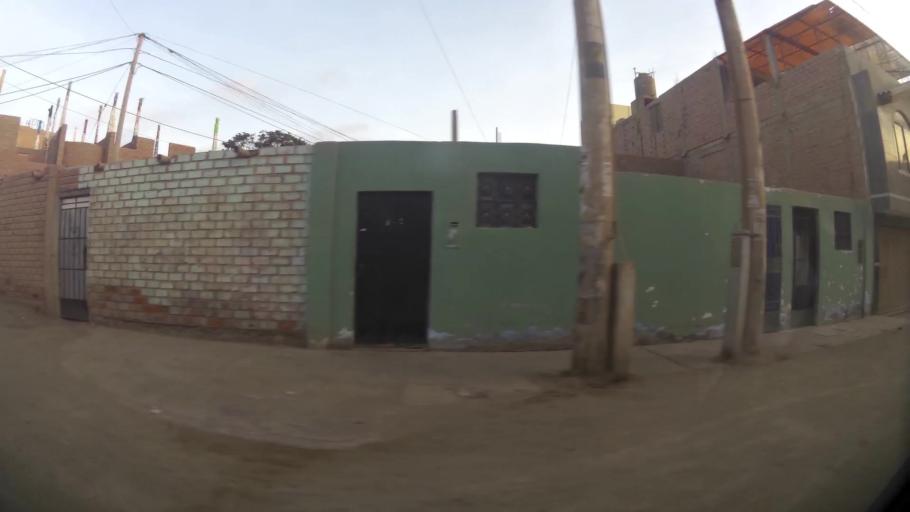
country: PE
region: Lima
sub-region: Huaura
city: Huacho
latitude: -11.1186
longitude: -77.6094
